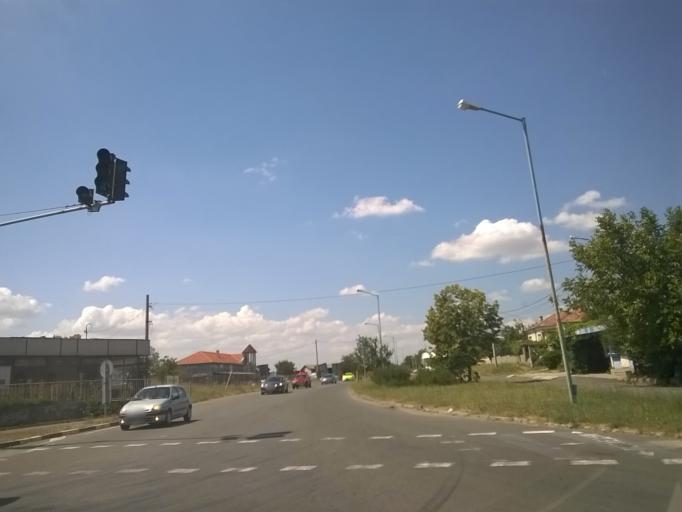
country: BG
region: Burgas
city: Aheloy
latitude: 42.6547
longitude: 27.5678
